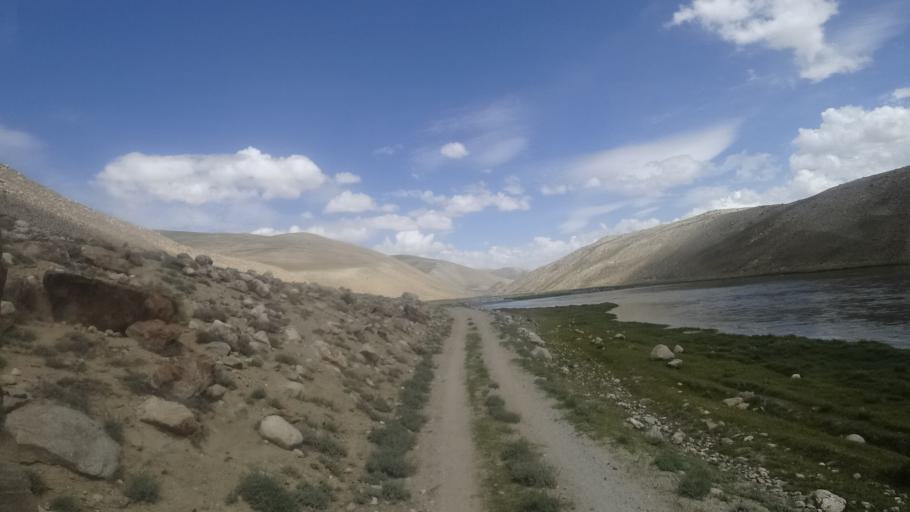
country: TJ
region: Gorno-Badakhshan
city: Murghob
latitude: 37.4735
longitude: 73.4481
